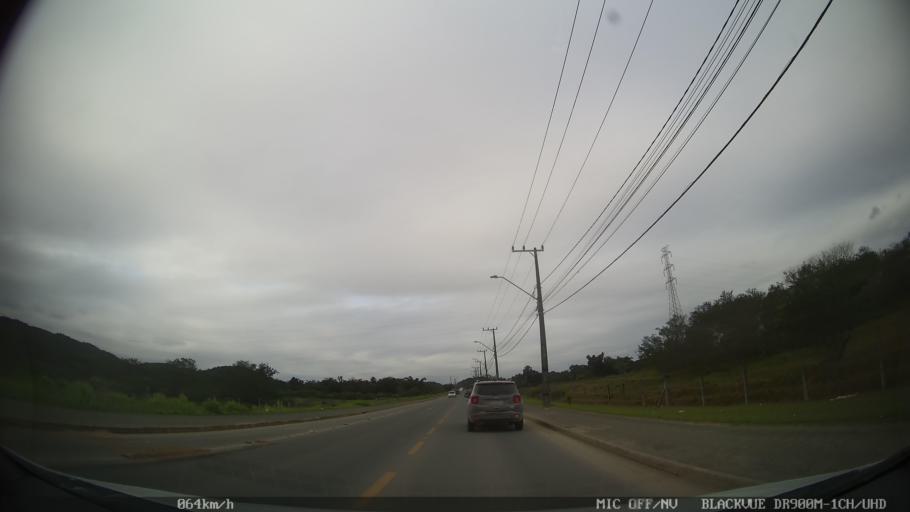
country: BR
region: Santa Catarina
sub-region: Joinville
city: Joinville
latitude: -26.3377
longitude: -48.8923
